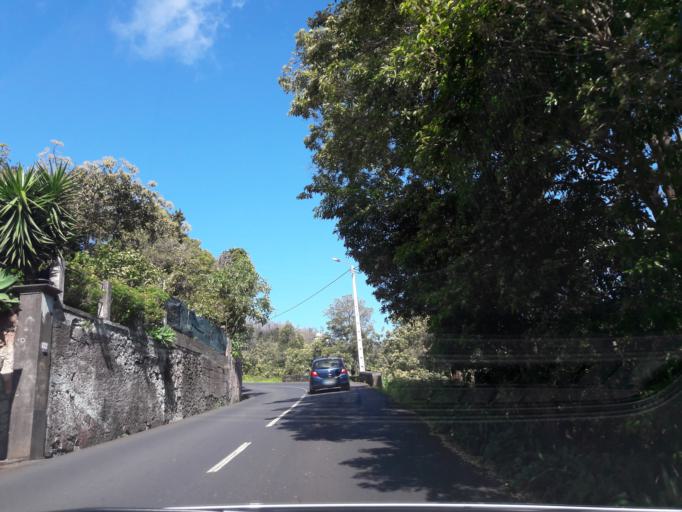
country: PT
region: Madeira
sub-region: Funchal
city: Nossa Senhora do Monte
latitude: 32.6743
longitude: -16.9068
